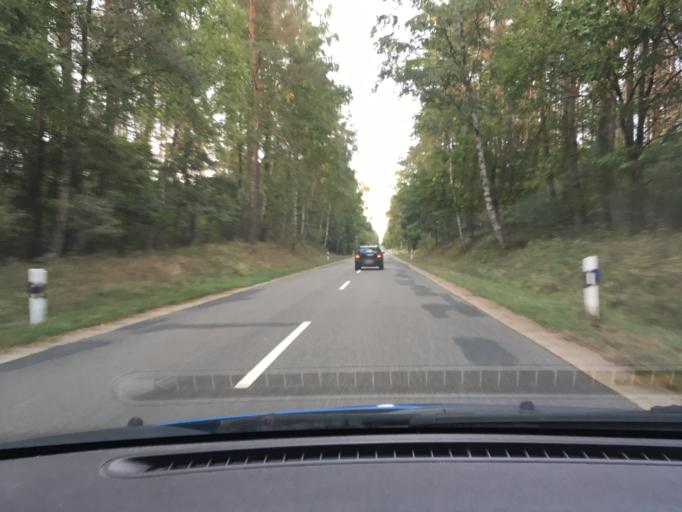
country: DE
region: Lower Saxony
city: Bispingen
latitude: 53.0802
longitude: 10.0362
